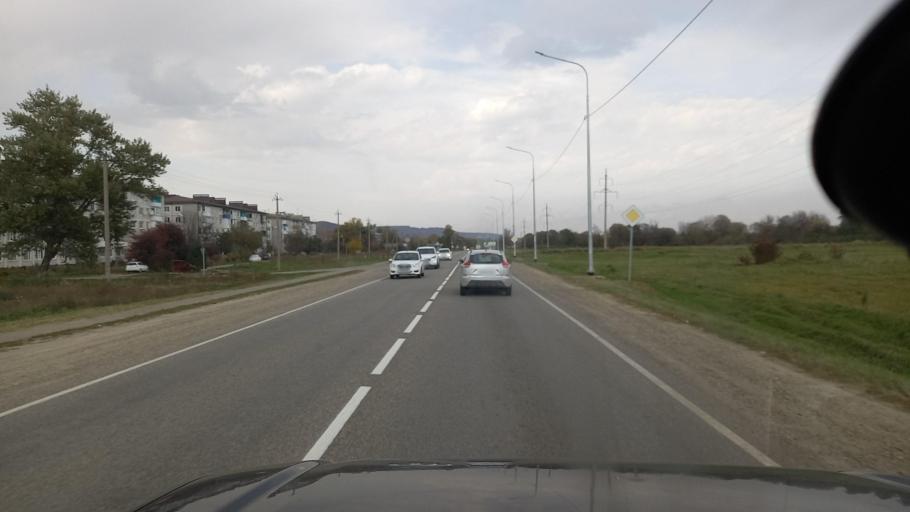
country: RU
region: Krasnodarskiy
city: Shedok
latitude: 44.1735
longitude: 40.8410
